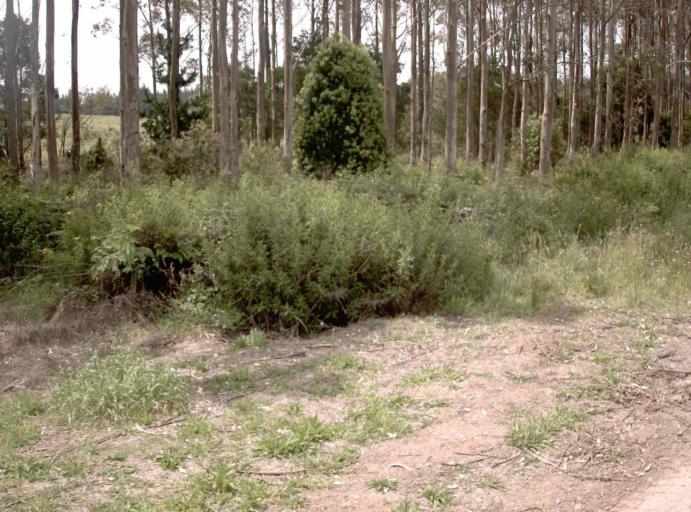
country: AU
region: Victoria
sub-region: Latrobe
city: Traralgon
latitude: -38.4050
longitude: 146.6406
